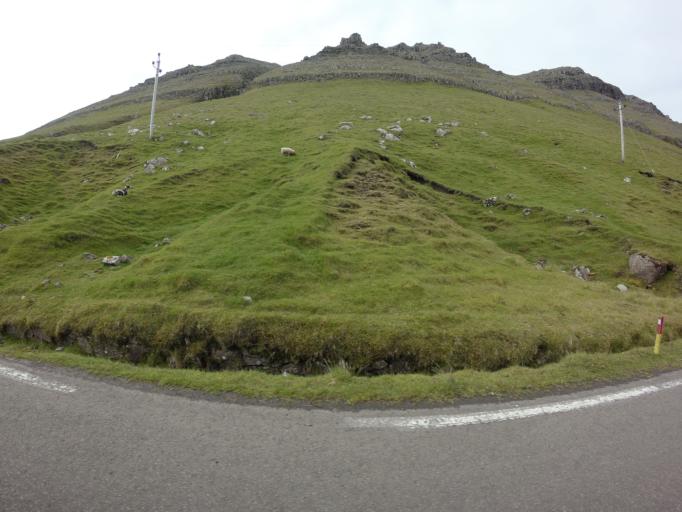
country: FO
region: Suduroy
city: Tvoroyri
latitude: 61.5774
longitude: -6.9390
